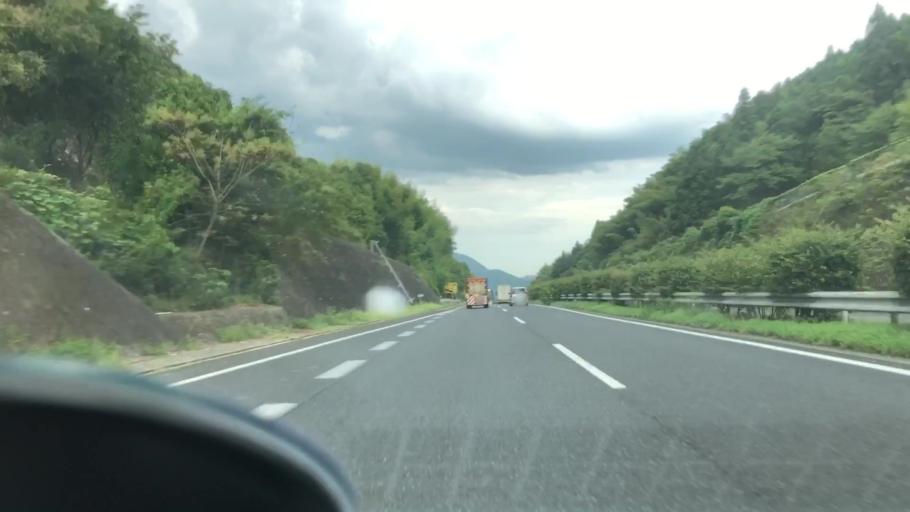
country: JP
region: Hyogo
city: Yamazakicho-nakabirose
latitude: 34.9750
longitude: 134.6468
